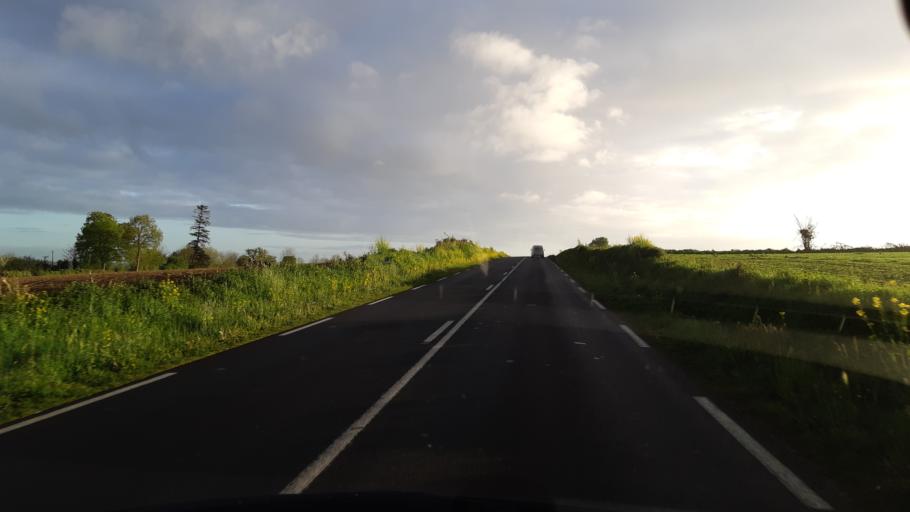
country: FR
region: Lower Normandy
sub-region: Departement de la Manche
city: Agneaux
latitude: 49.0374
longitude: -1.1327
